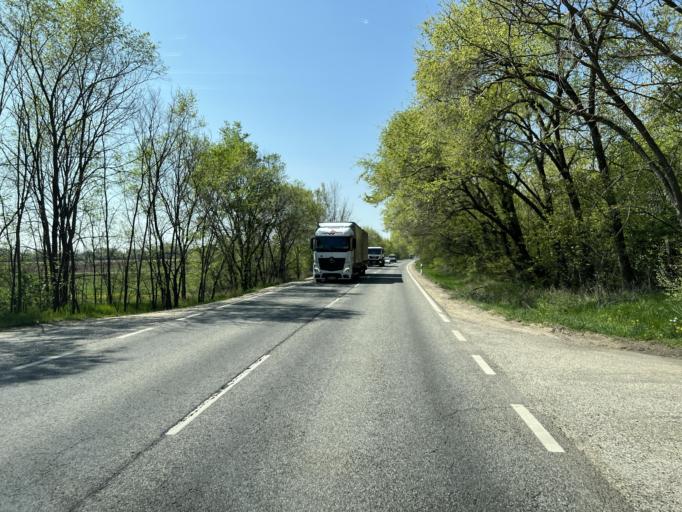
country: HU
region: Pest
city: Ocsa
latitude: 47.3100
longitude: 19.1967
